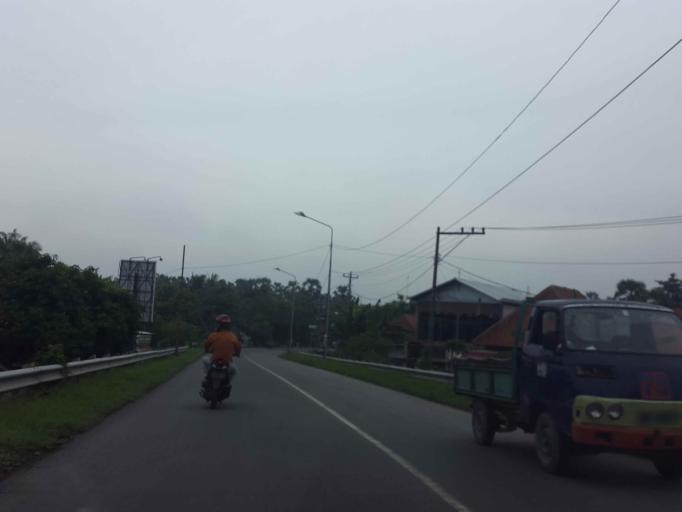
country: ID
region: Central Java
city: Semarang
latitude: -6.9846
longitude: 110.4742
